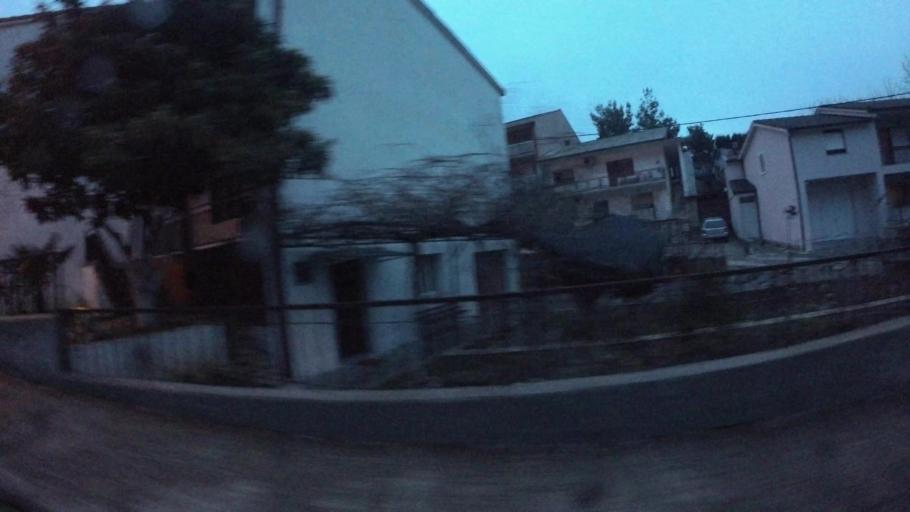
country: BA
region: Federation of Bosnia and Herzegovina
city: Rodoc
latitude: 43.3236
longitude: 17.8184
